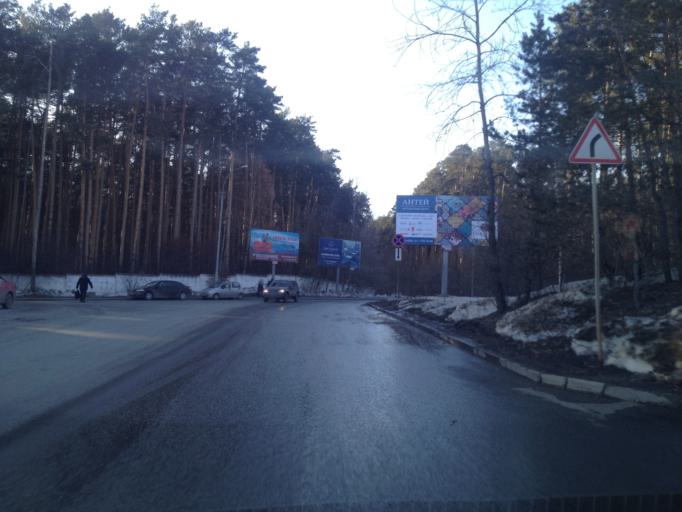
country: RU
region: Sverdlovsk
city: Sovkhoznyy
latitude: 56.8141
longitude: 60.5356
